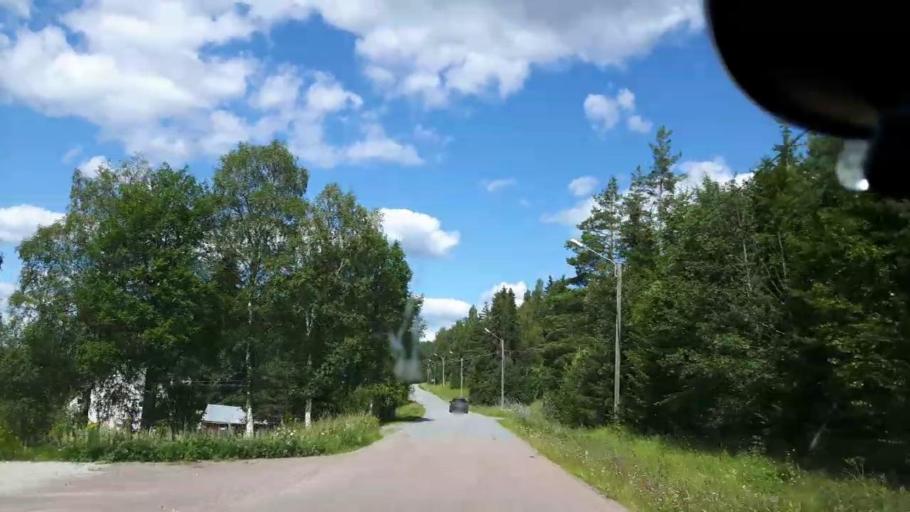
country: SE
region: Jaemtland
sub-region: Ragunda Kommun
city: Hammarstrand
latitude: 62.9469
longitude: 16.6892
